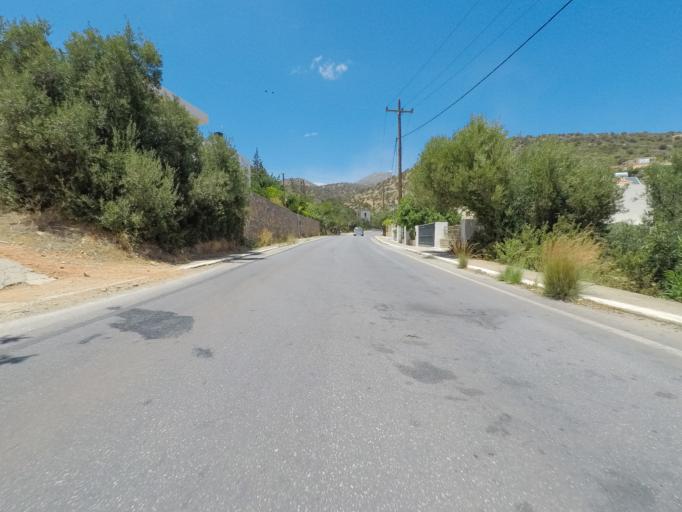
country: GR
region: Crete
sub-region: Nomos Lasithiou
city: Agios Nikolaos
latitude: 35.2180
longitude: 25.7104
